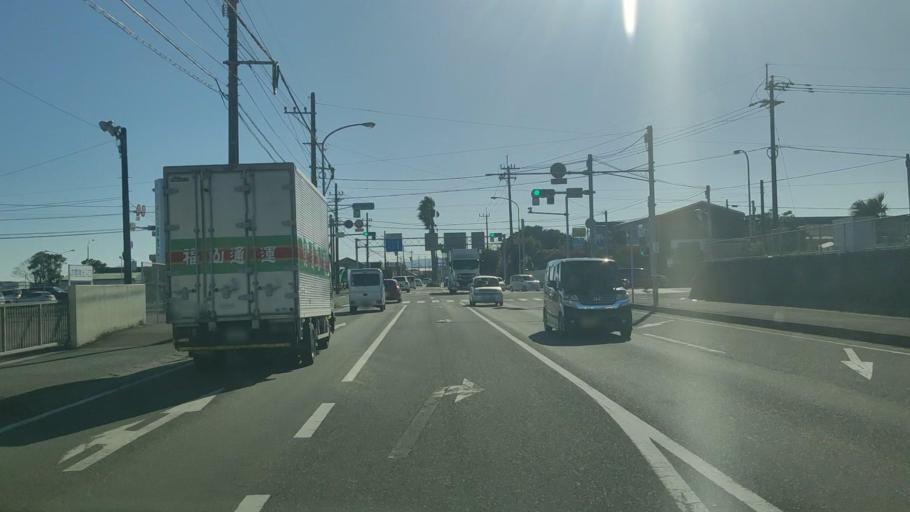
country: JP
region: Miyazaki
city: Miyazaki-shi
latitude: 31.9400
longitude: 131.4570
